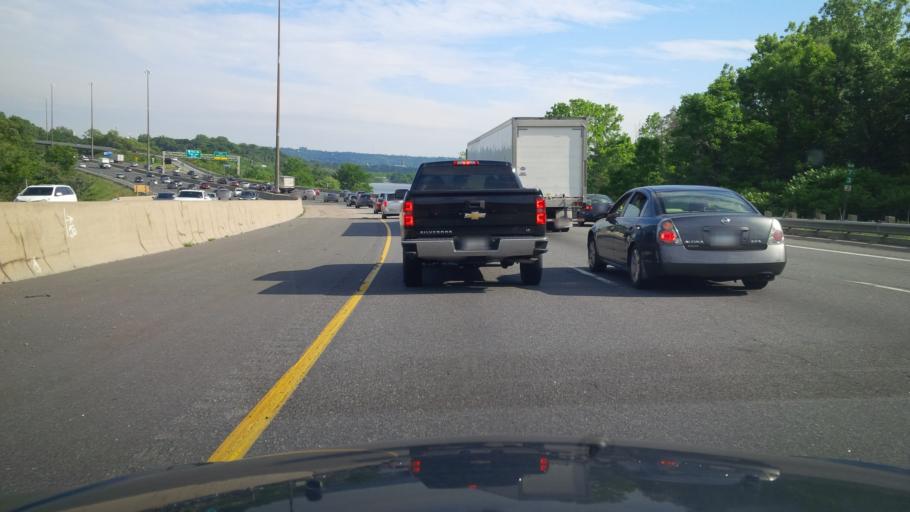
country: CA
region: Ontario
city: Hamilton
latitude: 43.2871
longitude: -79.8972
